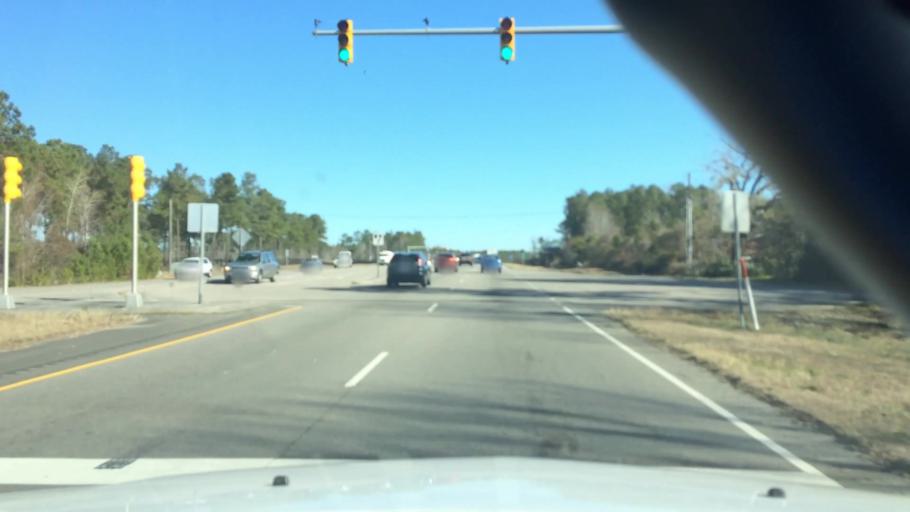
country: US
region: North Carolina
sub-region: Brunswick County
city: Bolivia
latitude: 34.0288
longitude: -78.2591
